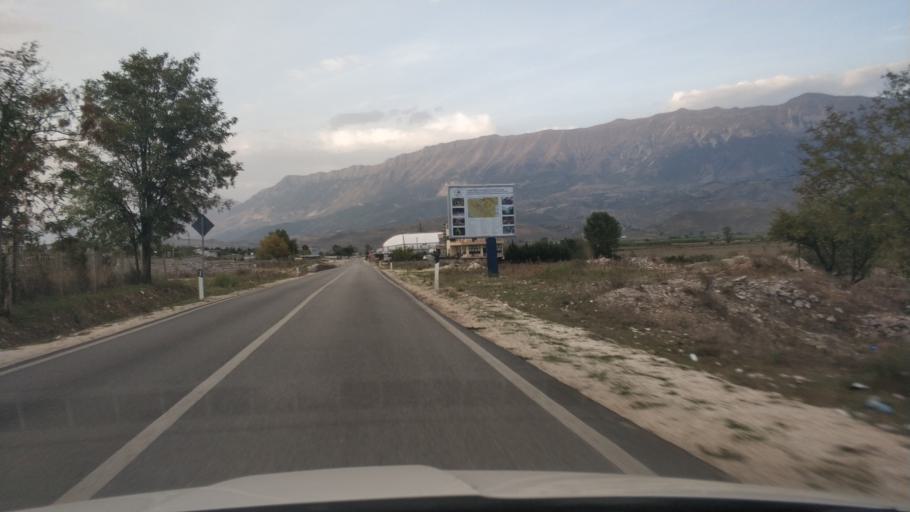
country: AL
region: Gjirokaster
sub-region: Rrethi i Gjirokastres
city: Dervician
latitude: 40.0464
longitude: 20.1766
